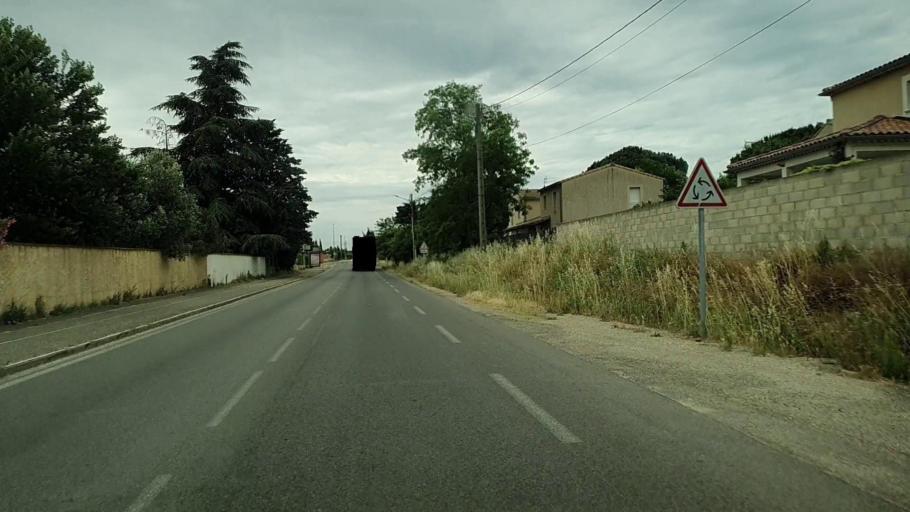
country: FR
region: Languedoc-Roussillon
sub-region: Departement du Gard
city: Bagnols-sur-Ceze
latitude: 44.1423
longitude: 4.6093
